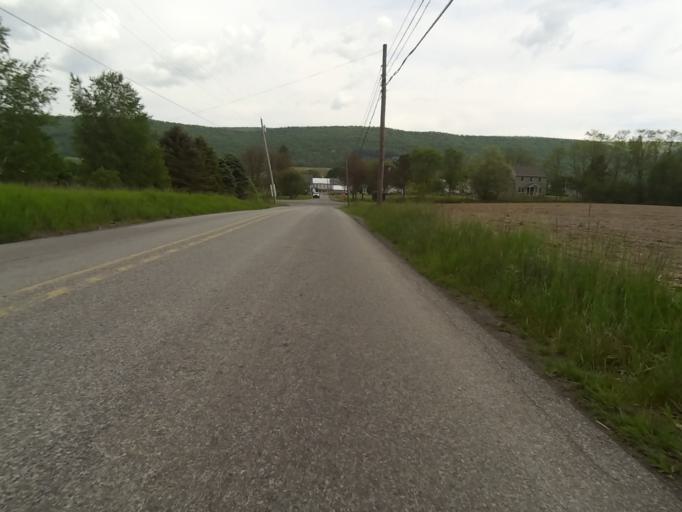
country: US
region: Pennsylvania
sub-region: Centre County
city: Zion
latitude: 40.9623
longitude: -77.6119
